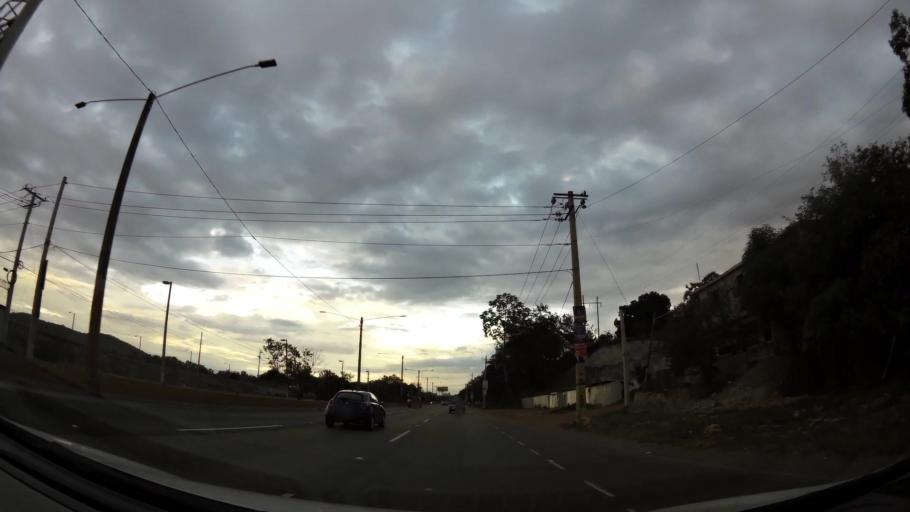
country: DO
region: Santo Domingo
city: Santo Domingo Oeste
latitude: 18.5615
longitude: -70.0658
